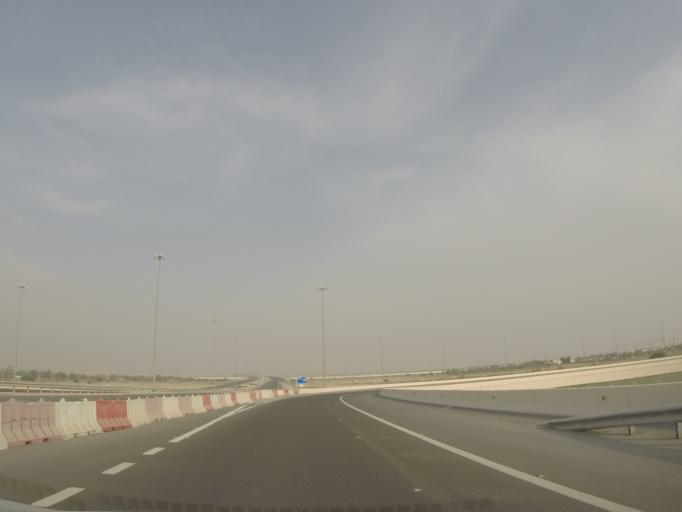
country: AE
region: Abu Dhabi
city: Abu Dhabi
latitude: 24.6935
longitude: 54.7799
